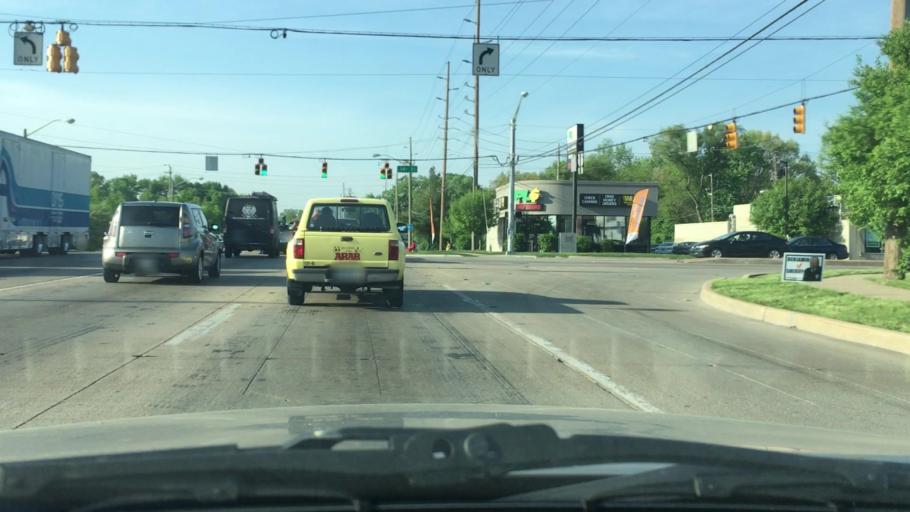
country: US
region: Indiana
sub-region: Marion County
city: Broad Ripple
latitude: 39.8257
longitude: -86.1219
